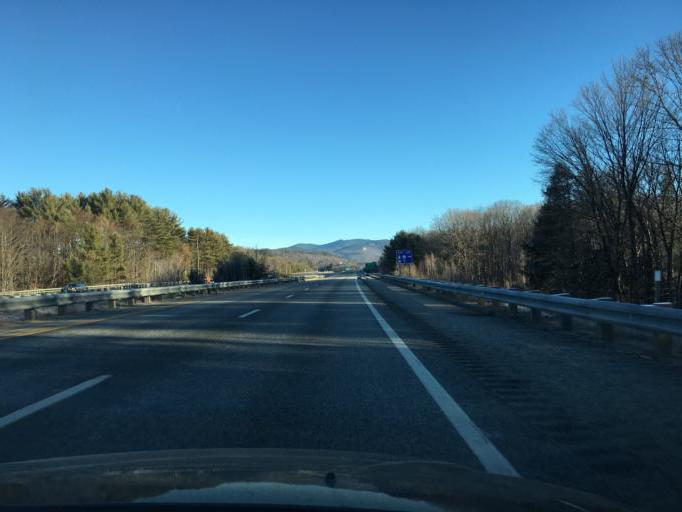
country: US
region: New Hampshire
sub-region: Grafton County
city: Thornton
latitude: 43.8378
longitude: -71.6515
